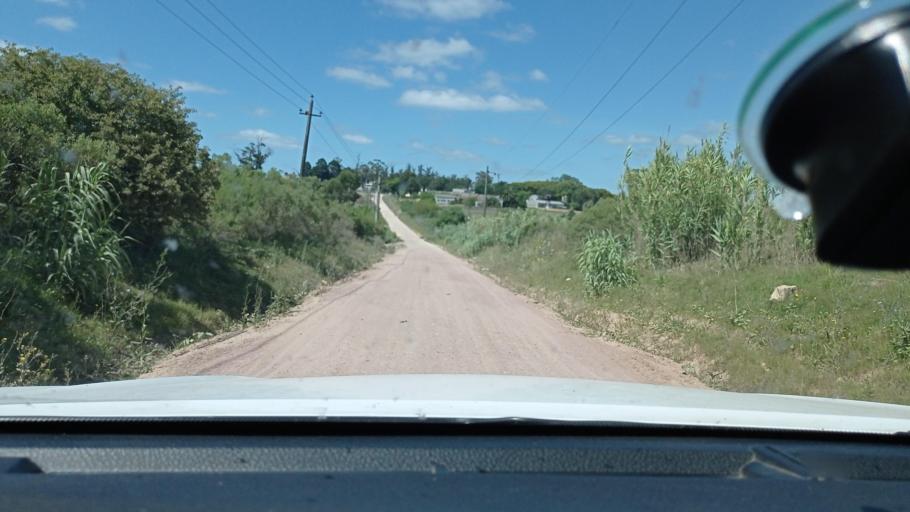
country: UY
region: Canelones
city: Pando
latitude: -34.7288
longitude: -55.9745
